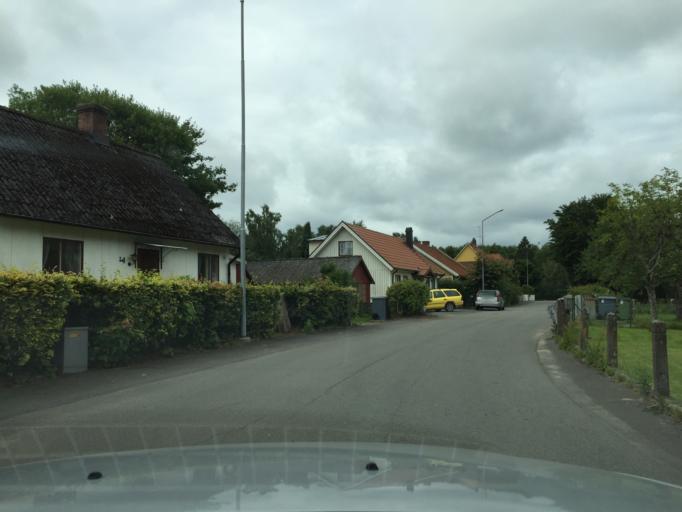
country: SE
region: Skane
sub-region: Hassleholms Kommun
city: Sosdala
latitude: 56.0336
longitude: 13.6746
